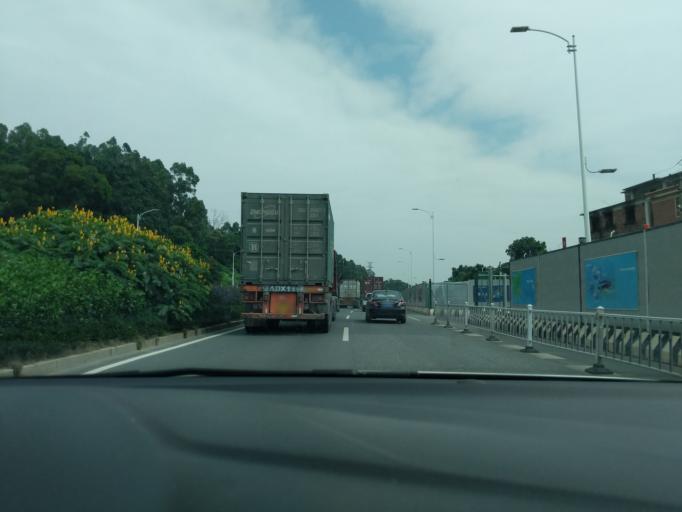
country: CN
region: Guangdong
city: Nansha
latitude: 22.7551
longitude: 113.5722
